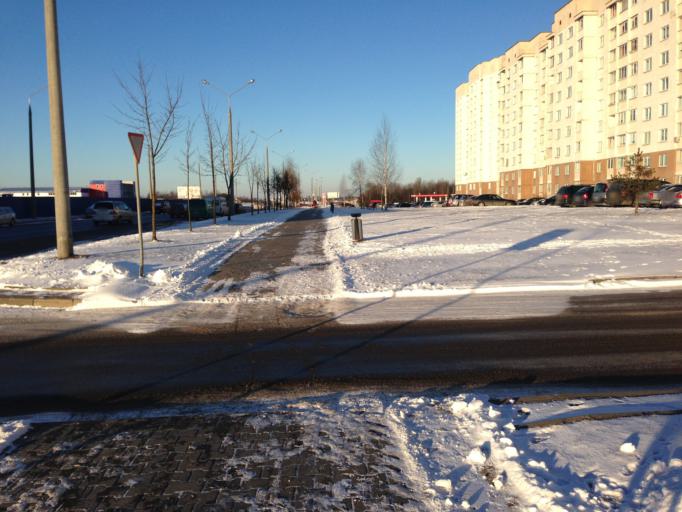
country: BY
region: Grodnenskaya
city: Hrodna
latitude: 53.7137
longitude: 23.8401
